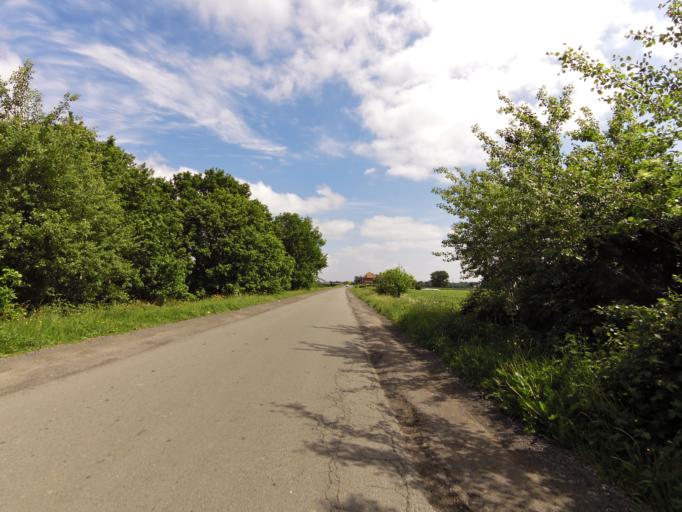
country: BE
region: Flanders
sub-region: Provincie Oost-Vlaanderen
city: Knesselare
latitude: 51.1182
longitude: 3.3888
